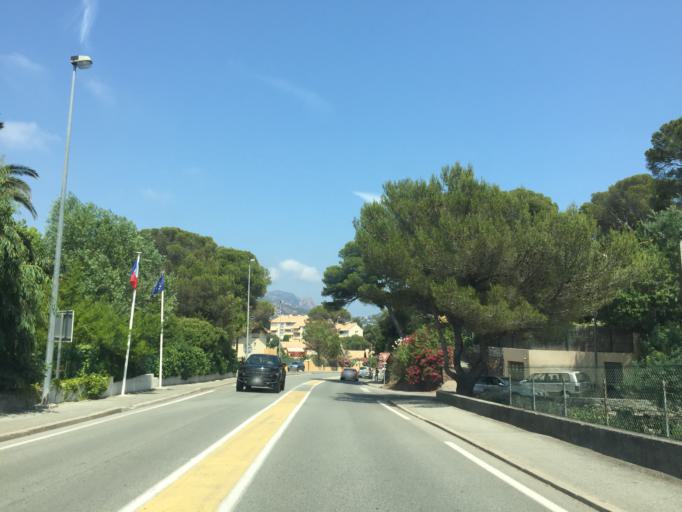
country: FR
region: Provence-Alpes-Cote d'Azur
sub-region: Departement du Var
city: Saint-Raphael
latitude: 43.4193
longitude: 6.8525
